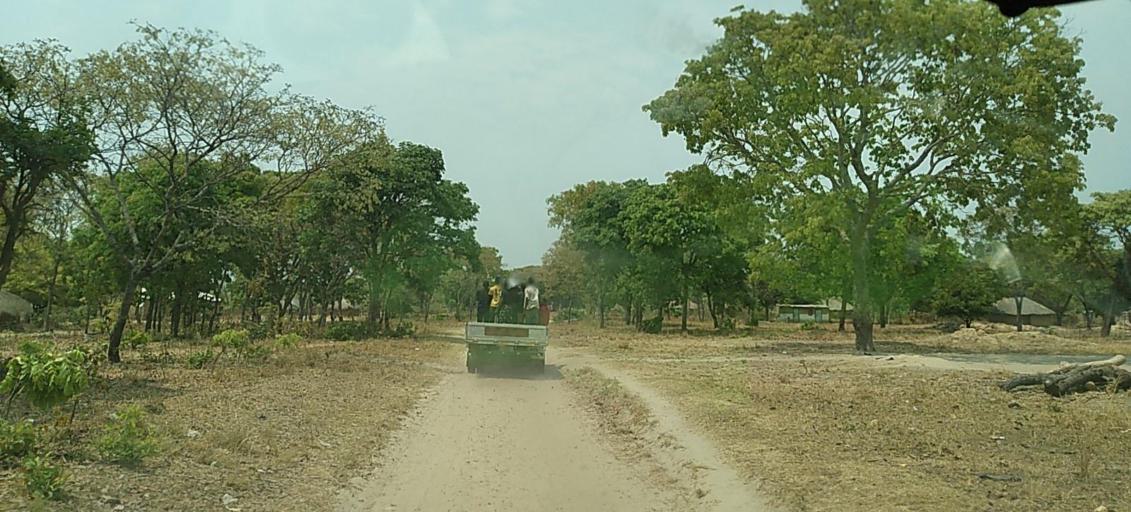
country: ZM
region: North-Western
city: Kabompo
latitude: -13.4892
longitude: 24.4621
